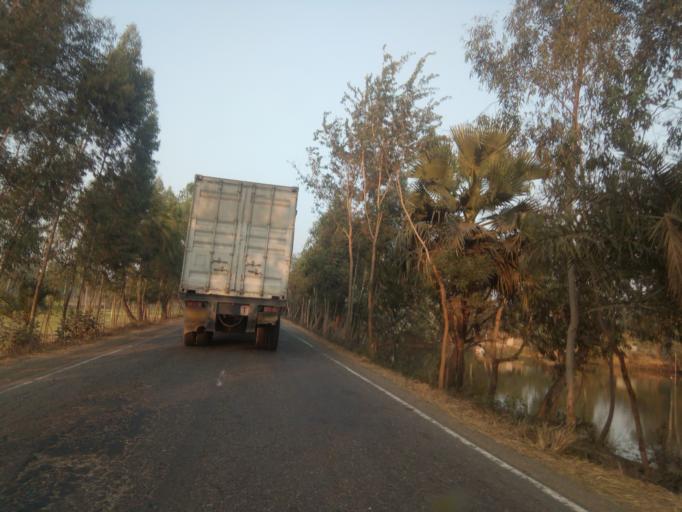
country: BD
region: Rajshahi
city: Par Naogaon
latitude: 24.5476
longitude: 89.1895
